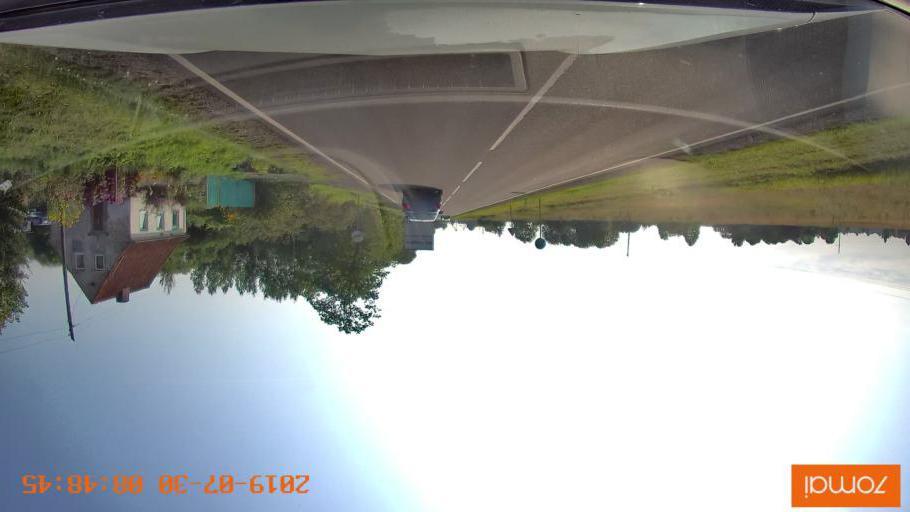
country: RU
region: Kaliningrad
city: Chernyakhovsk
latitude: 54.6158
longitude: 21.9100
